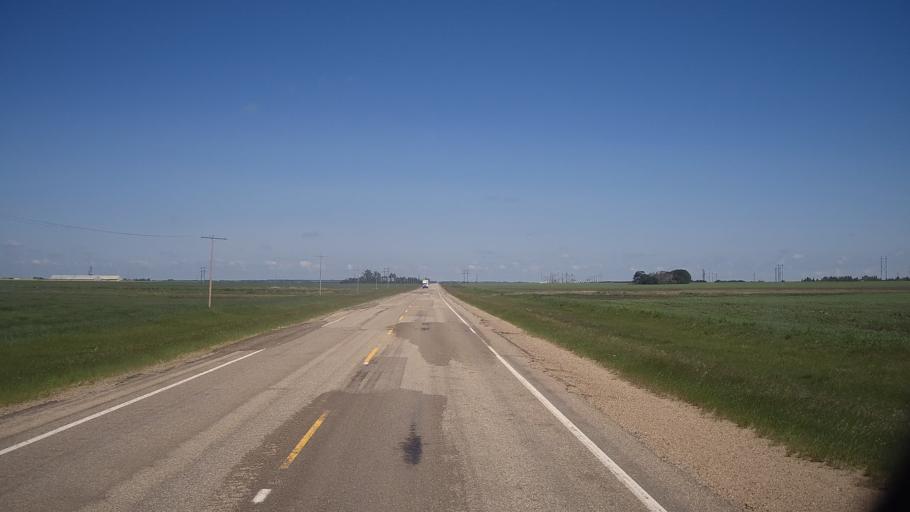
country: CA
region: Saskatchewan
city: Saskatoon
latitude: 51.9708
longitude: -106.0752
